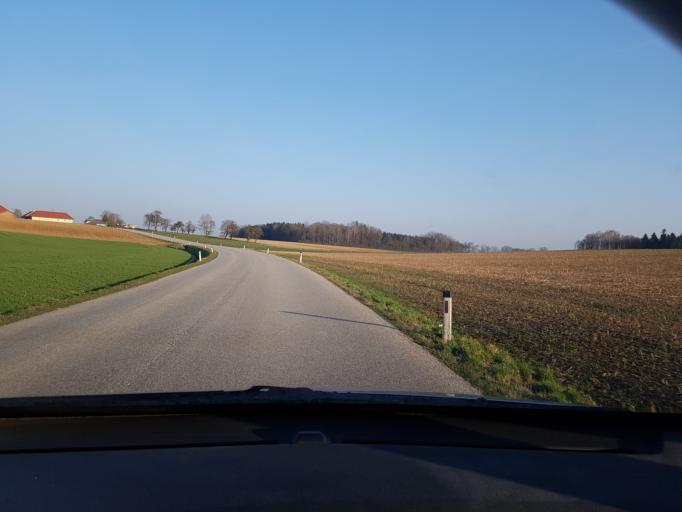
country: AT
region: Upper Austria
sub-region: Politischer Bezirk Steyr-Land
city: Sierning
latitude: 48.1244
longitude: 14.3008
